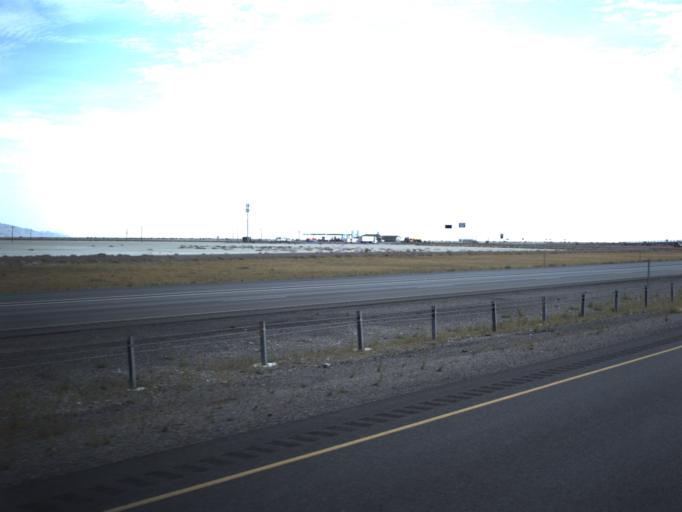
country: US
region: Utah
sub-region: Tooele County
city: Wendover
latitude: 40.7428
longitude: -113.9773
